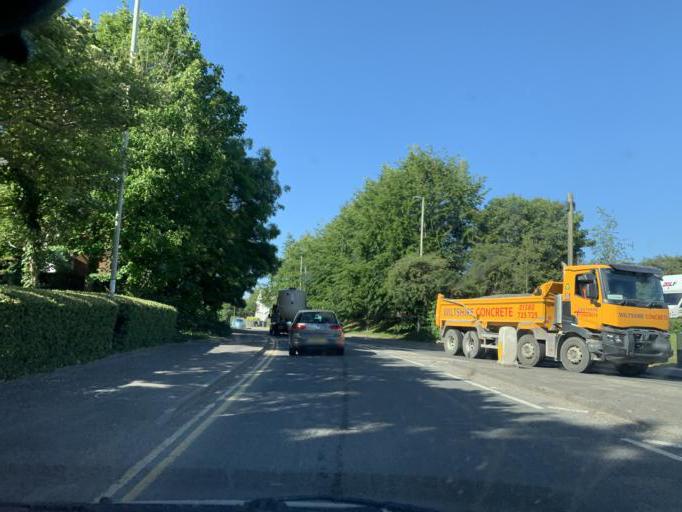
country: GB
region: England
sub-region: Wiltshire
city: Devizes
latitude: 51.3638
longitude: -1.9729
